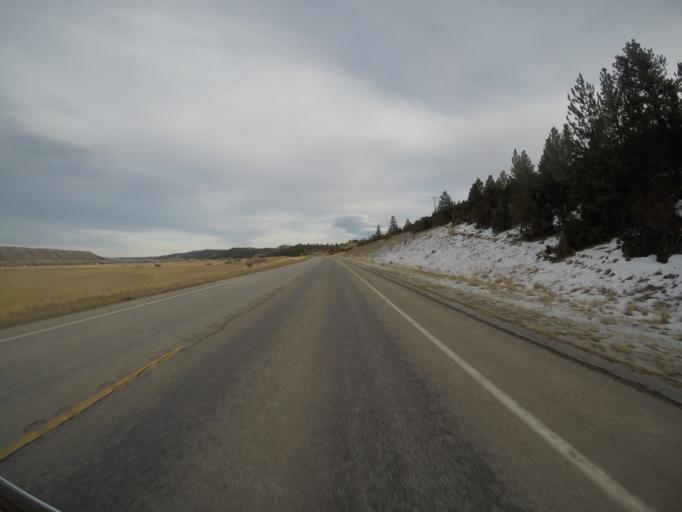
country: US
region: Montana
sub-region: Stillwater County
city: Absarokee
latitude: 45.5437
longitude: -109.3881
